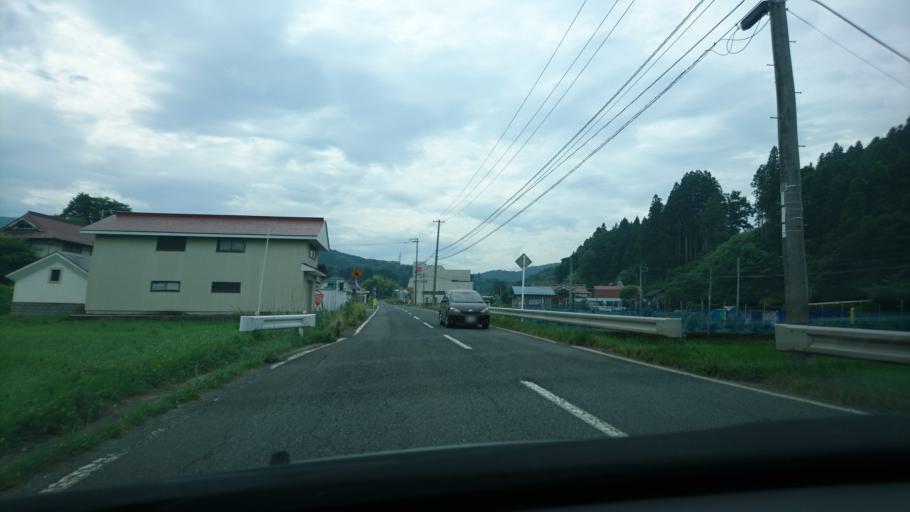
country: JP
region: Iwate
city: Ichinoseki
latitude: 38.9011
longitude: 141.4247
